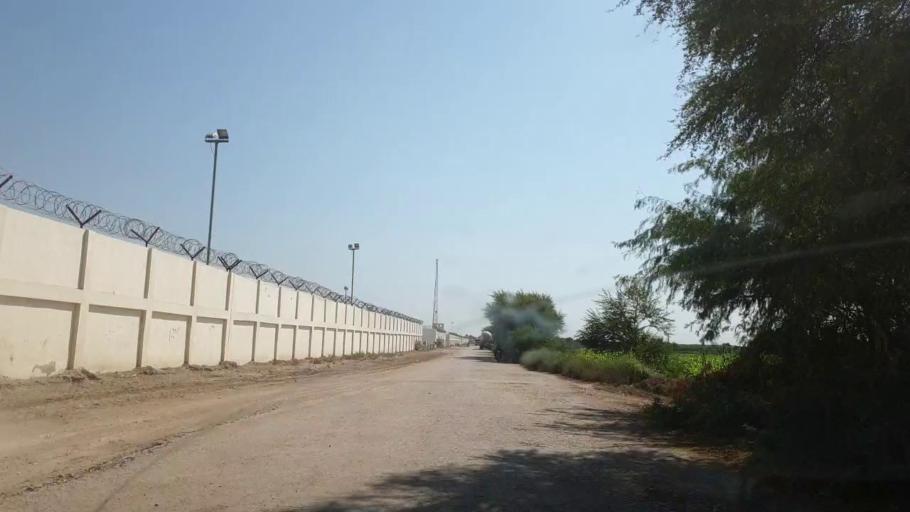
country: PK
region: Sindh
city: Tando Jam
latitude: 25.3884
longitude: 68.5790
